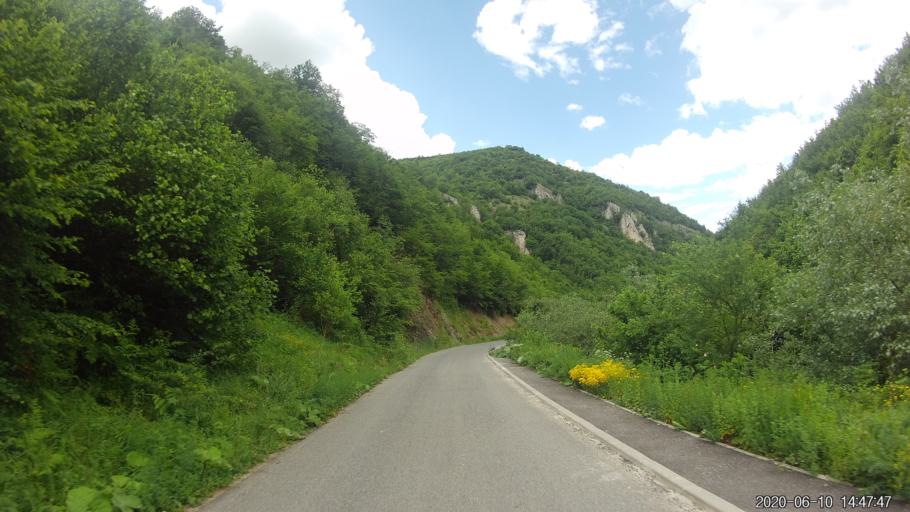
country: XK
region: Prizren
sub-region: Komuna e Therandes
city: Budakovo
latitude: 42.3889
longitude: 20.9615
